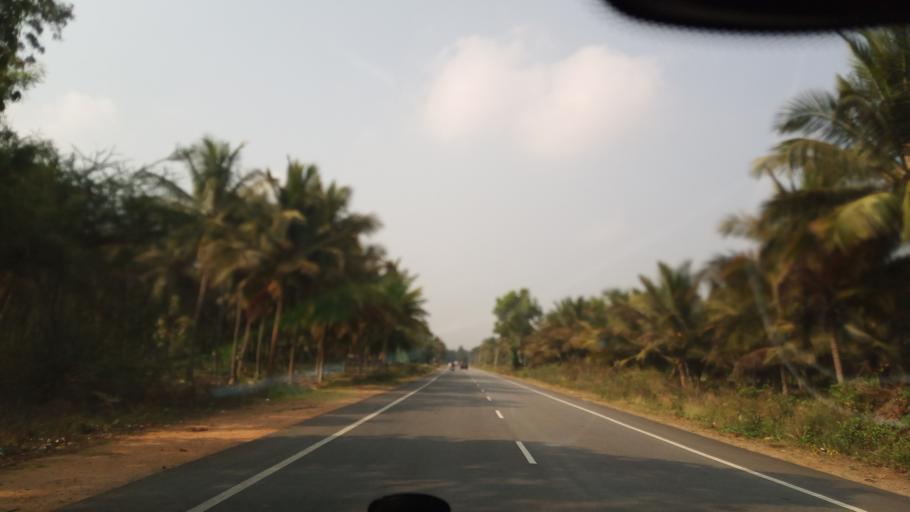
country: IN
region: Karnataka
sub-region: Mandya
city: Nagamangala
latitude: 12.7733
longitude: 76.7406
